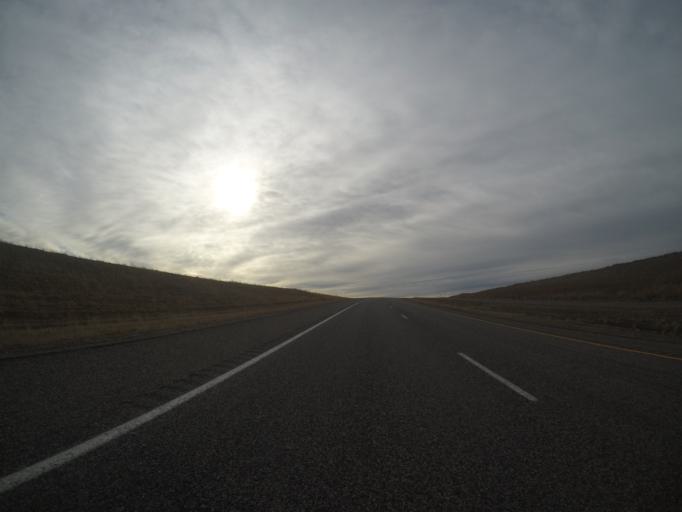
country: US
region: Montana
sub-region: Yellowstone County
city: Laurel
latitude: 45.6013
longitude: -108.8231
